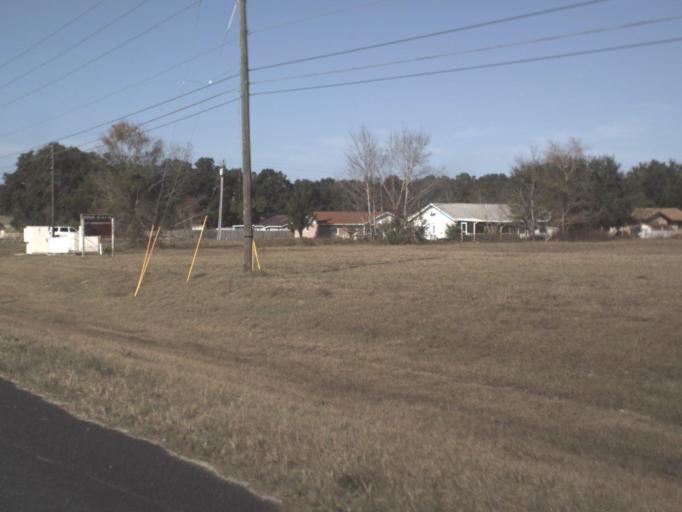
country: US
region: Florida
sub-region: Marion County
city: Belleview
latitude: 29.0257
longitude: -82.1377
